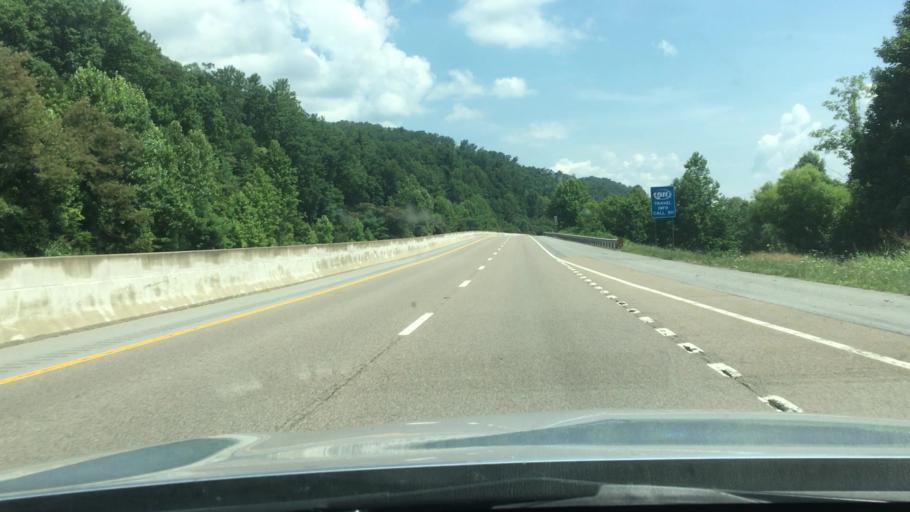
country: US
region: Tennessee
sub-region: Unicoi County
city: Banner Hill
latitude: 36.0900
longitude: -82.4859
